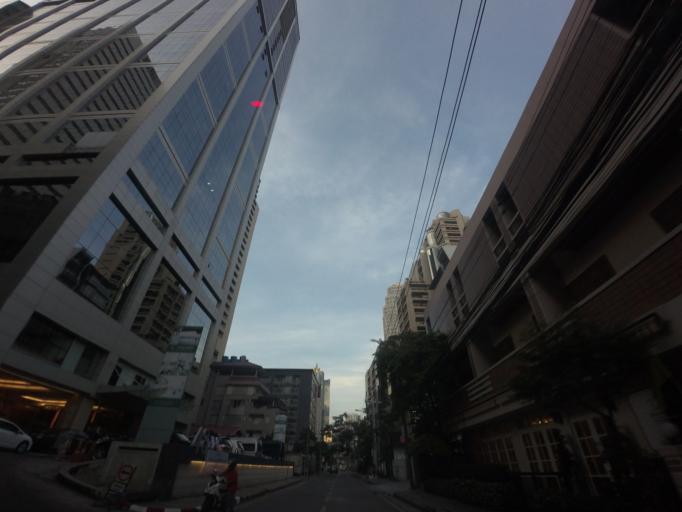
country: TH
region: Bangkok
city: Khlong Toei
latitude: 13.7328
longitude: 100.5610
